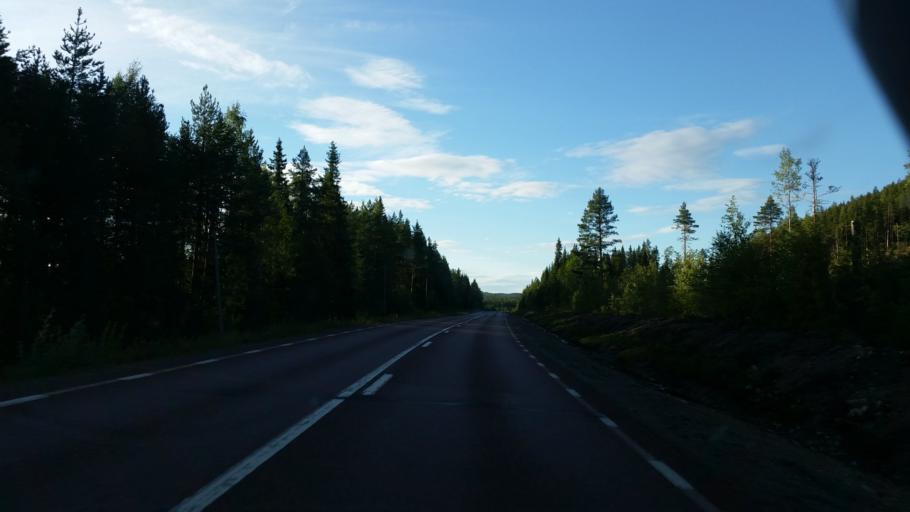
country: SE
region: Vaesterbotten
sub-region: Dorotea Kommun
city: Dorotea
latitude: 64.2005
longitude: 16.2876
